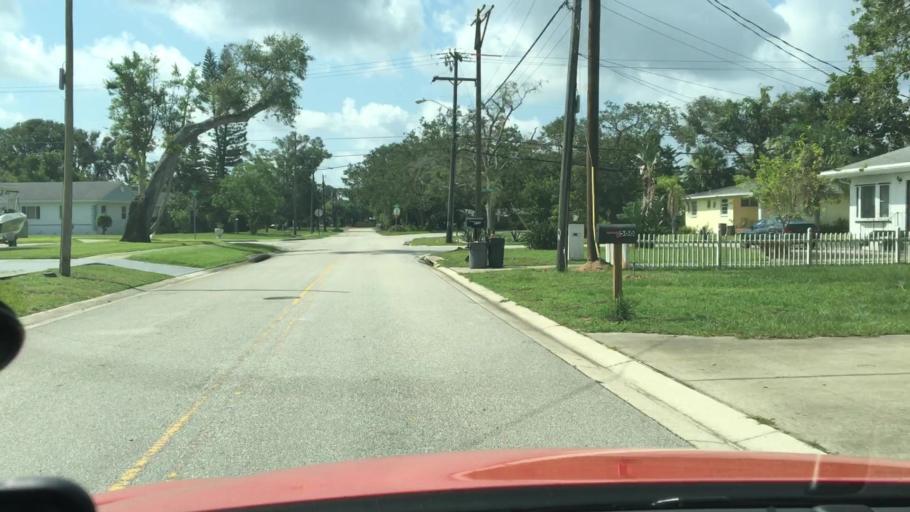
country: US
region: Florida
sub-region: Volusia County
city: Ormond Beach
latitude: 29.2703
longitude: -81.0516
